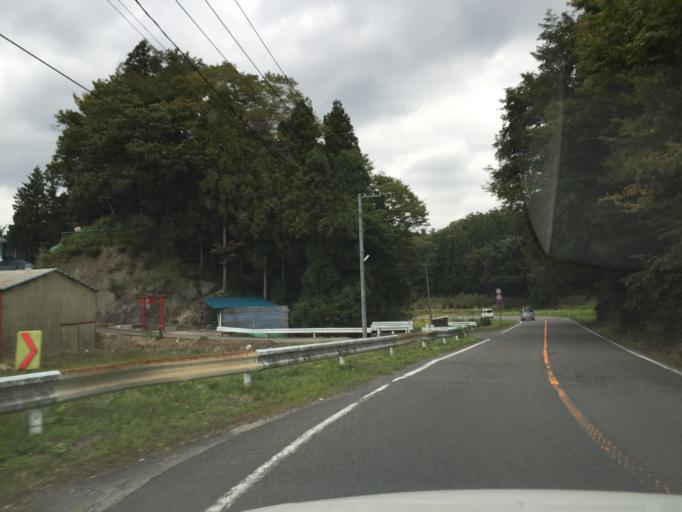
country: JP
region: Fukushima
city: Miharu
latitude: 37.4162
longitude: 140.5326
